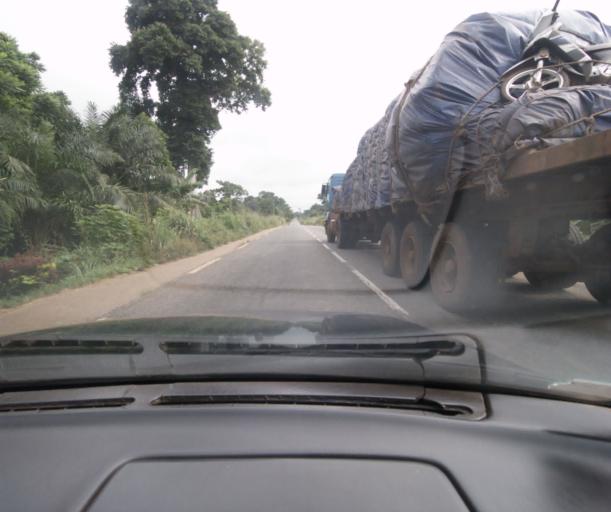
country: CM
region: Centre
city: Ombesa
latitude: 4.5914
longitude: 11.2625
